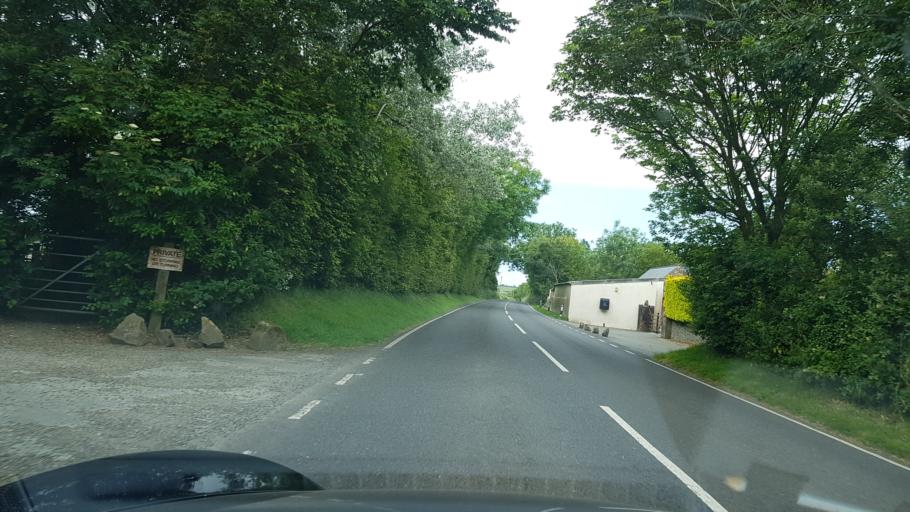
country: GB
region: Wales
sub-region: Pembrokeshire
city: Johnston
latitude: 51.7809
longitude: -5.0329
